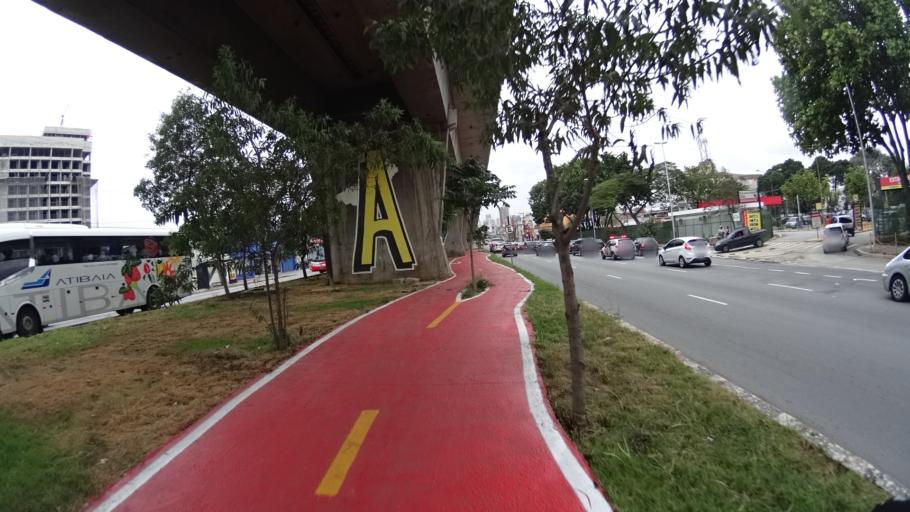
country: BR
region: Sao Paulo
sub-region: Sao Paulo
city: Sao Paulo
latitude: -23.5144
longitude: -46.6250
